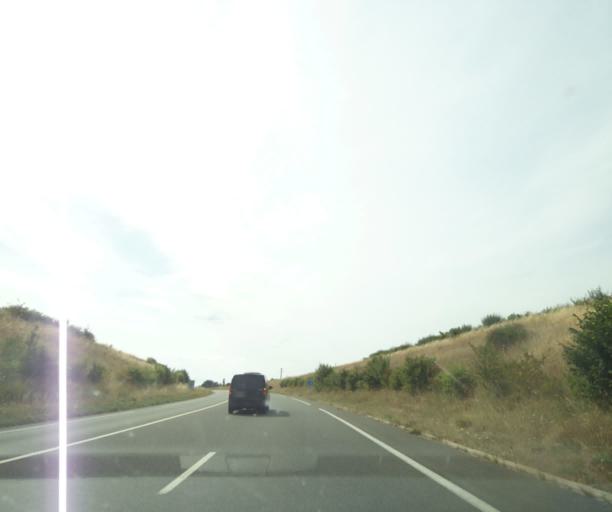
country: FR
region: Pays de la Loire
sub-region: Departement de la Sarthe
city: Luceau
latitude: 47.7120
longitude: 0.4084
